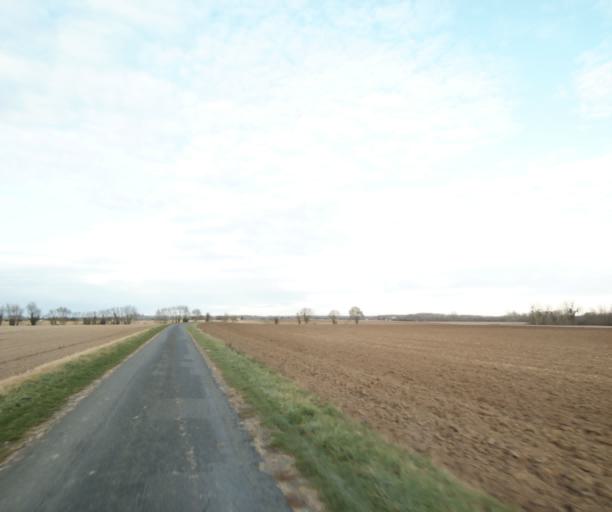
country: FR
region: Poitou-Charentes
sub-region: Departement de la Charente-Maritime
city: Les Gonds
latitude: 45.7006
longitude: -0.6175
